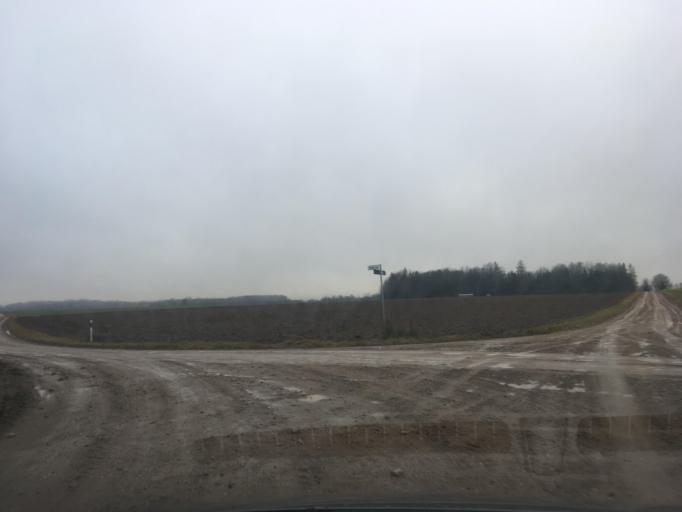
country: EE
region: Tartu
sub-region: Tartu linn
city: Tartu
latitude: 58.3975
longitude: 26.9205
